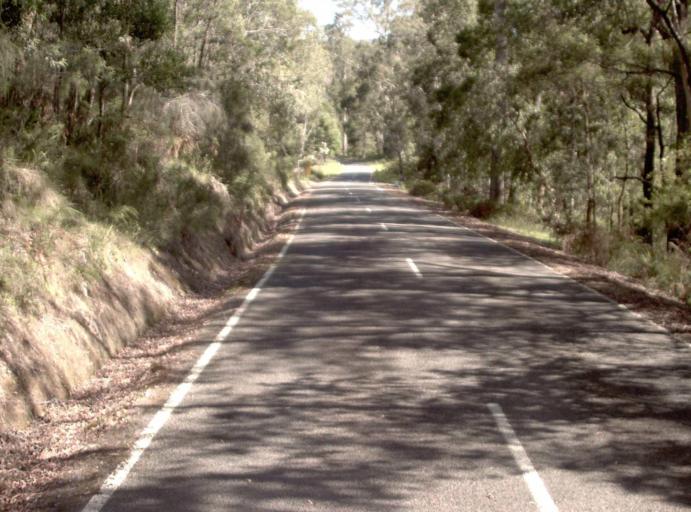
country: AU
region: New South Wales
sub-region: Bombala
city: Bombala
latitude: -37.3747
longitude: 148.6817
